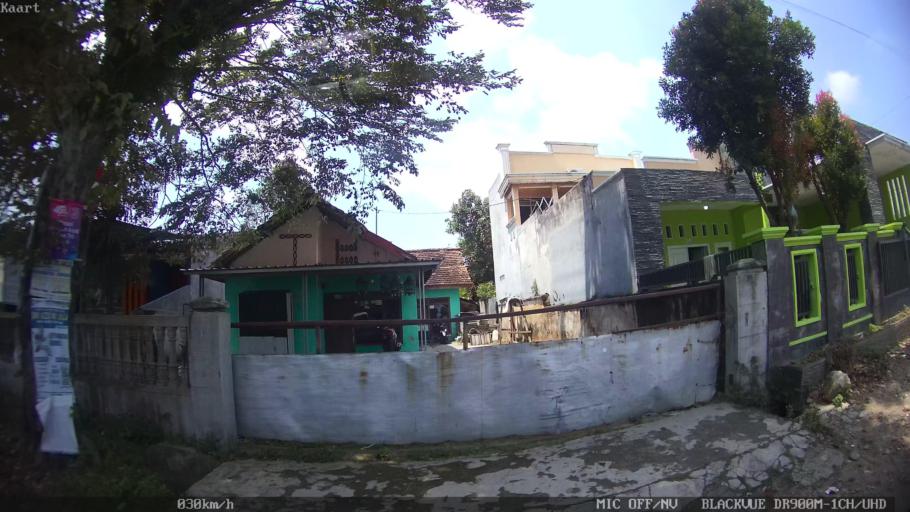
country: ID
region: Lampung
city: Kedaton
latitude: -5.3775
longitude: 105.2639
